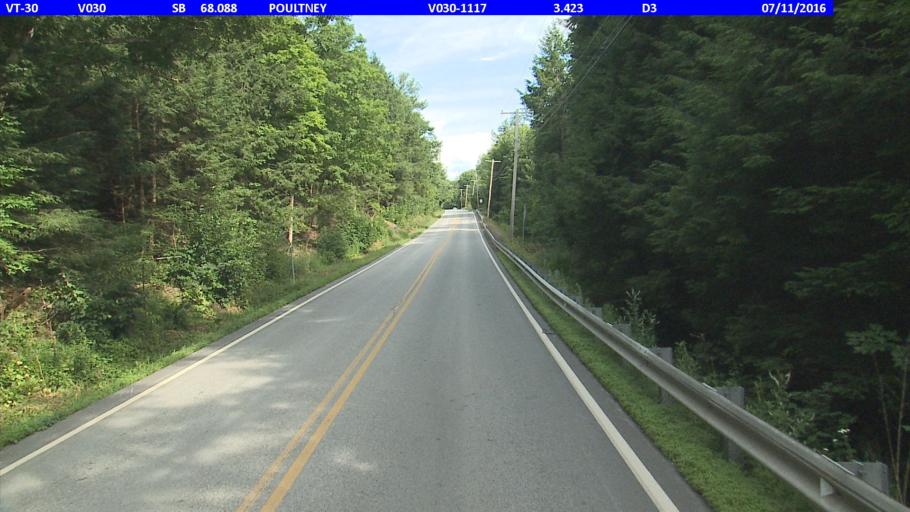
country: US
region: Vermont
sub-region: Rutland County
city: Poultney
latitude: 43.5088
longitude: -73.2160
